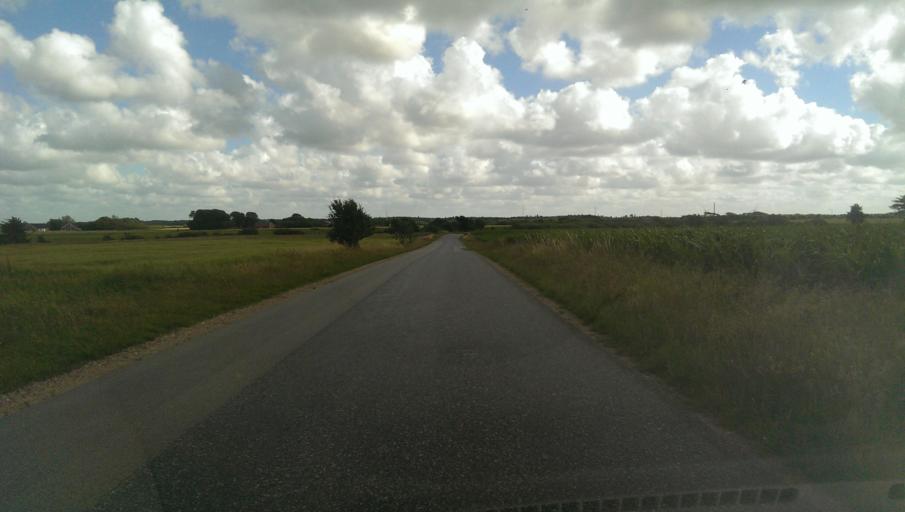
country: DK
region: South Denmark
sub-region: Esbjerg Kommune
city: Tjaereborg
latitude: 55.5112
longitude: 8.5768
